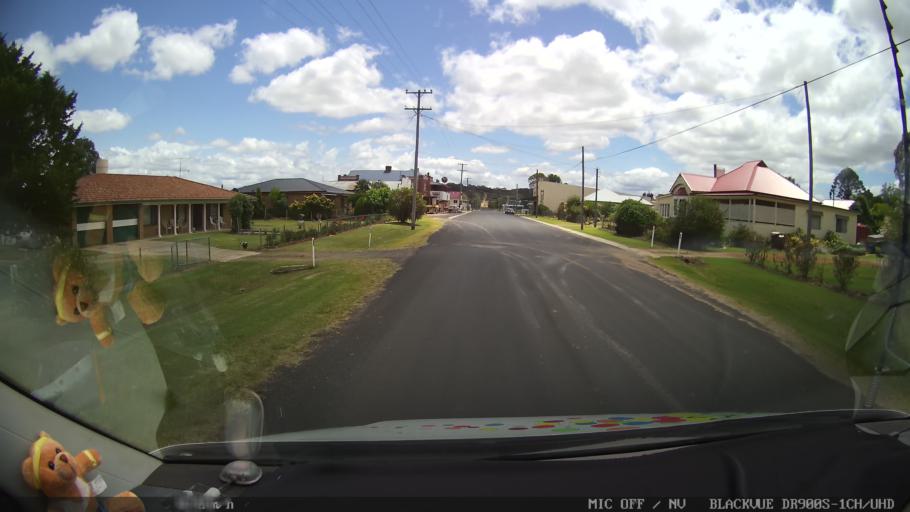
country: AU
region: New South Wales
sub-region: Glen Innes Severn
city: Glen Innes
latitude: -29.4461
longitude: 151.5979
